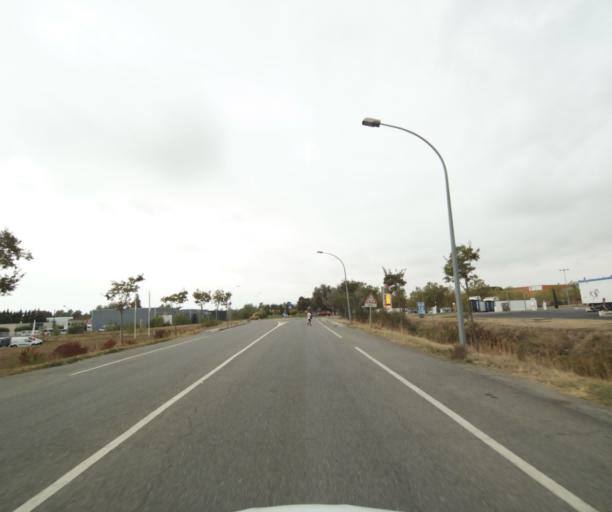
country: FR
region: Midi-Pyrenees
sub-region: Departement de la Haute-Garonne
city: Villefranche-de-Lauragais
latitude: 43.3989
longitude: 1.7030
